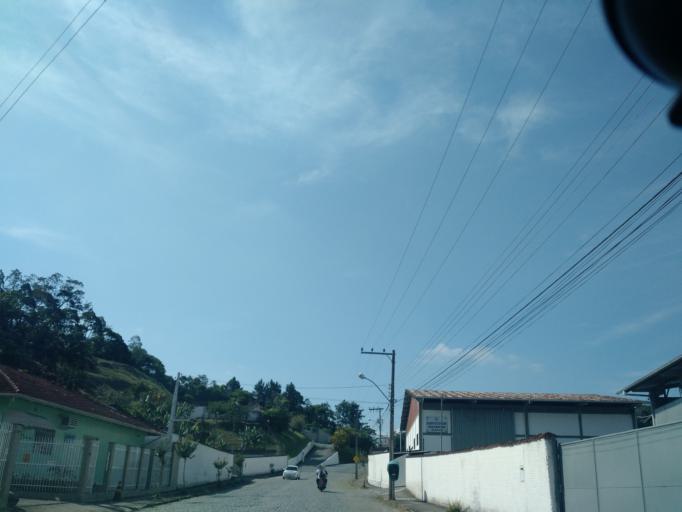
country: BR
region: Santa Catarina
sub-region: Jaragua Do Sul
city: Jaragua do Sul
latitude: -26.4981
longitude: -49.0987
